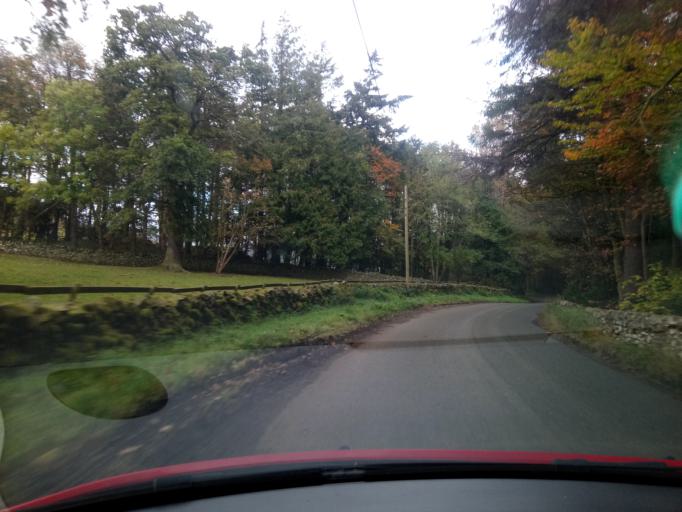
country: GB
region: Scotland
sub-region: The Scottish Borders
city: Peebles
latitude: 55.6340
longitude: -3.1470
